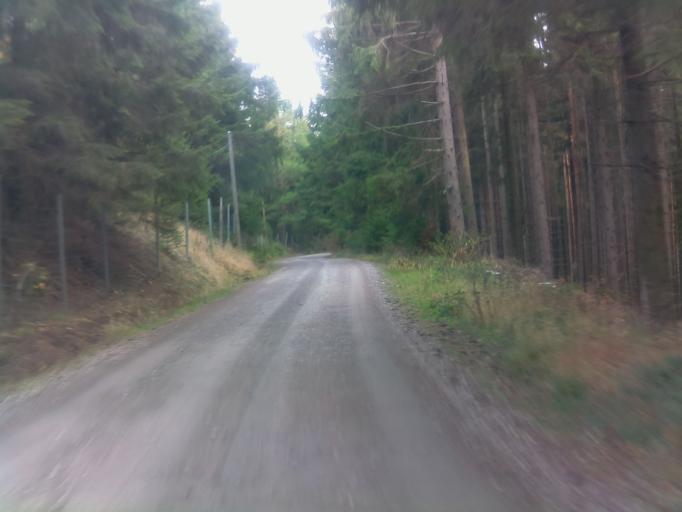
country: DE
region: Thuringia
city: Grafenhain
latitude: 50.8044
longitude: 10.6762
